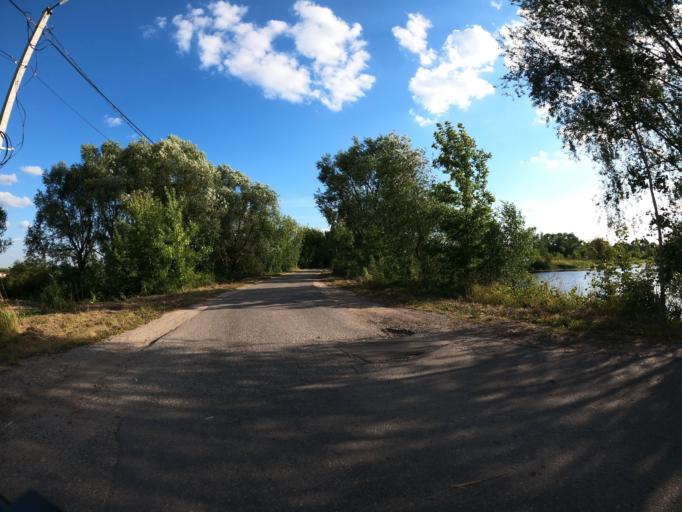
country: RU
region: Moskovskaya
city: Raduzhnyy
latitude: 55.1527
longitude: 38.7377
